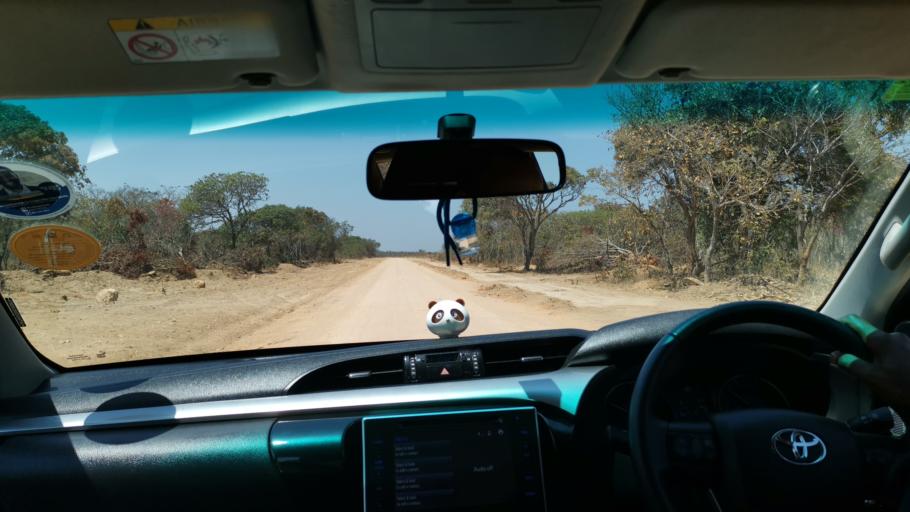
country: ZM
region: Central
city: Mkushi
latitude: -13.6522
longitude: 29.7519
